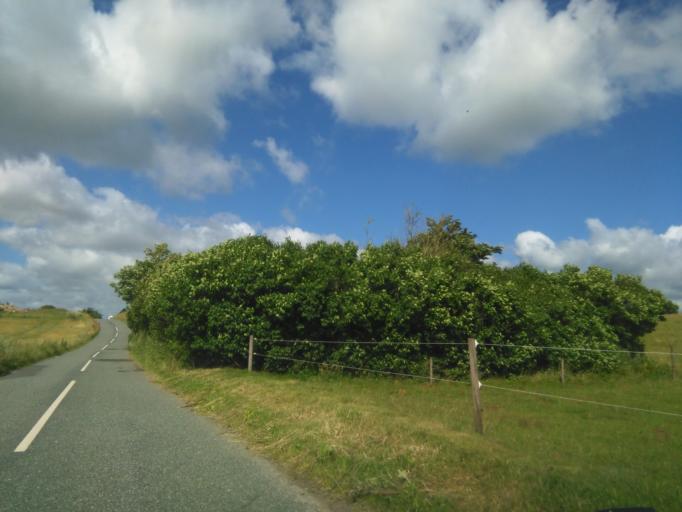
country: DK
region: Central Jutland
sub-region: Syddjurs Kommune
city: Ronde
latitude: 56.2269
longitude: 10.5192
